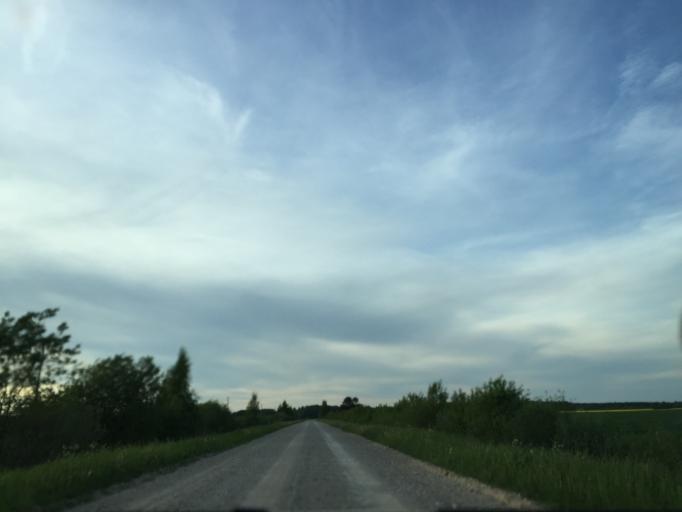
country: LV
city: Tireli
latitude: 56.7267
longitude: 23.5037
